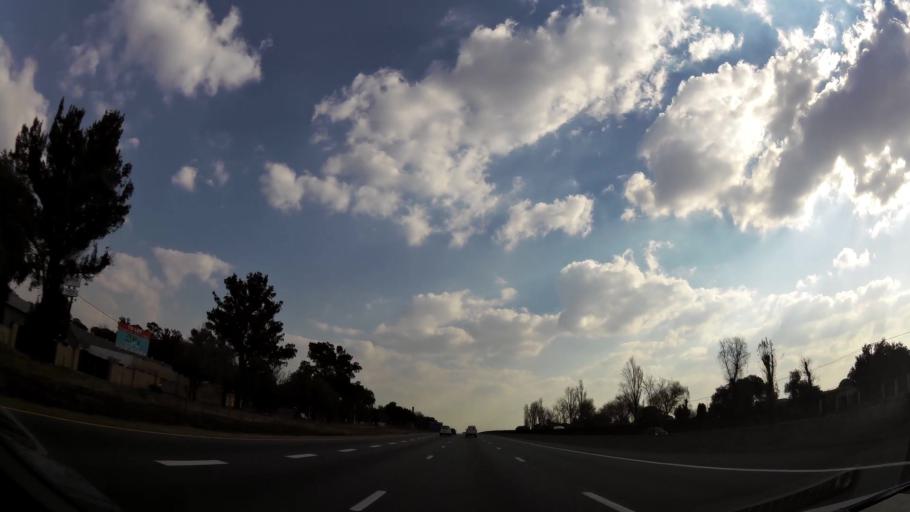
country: ZA
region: Gauteng
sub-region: Ekurhuleni Metropolitan Municipality
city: Germiston
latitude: -26.2544
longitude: 28.1943
